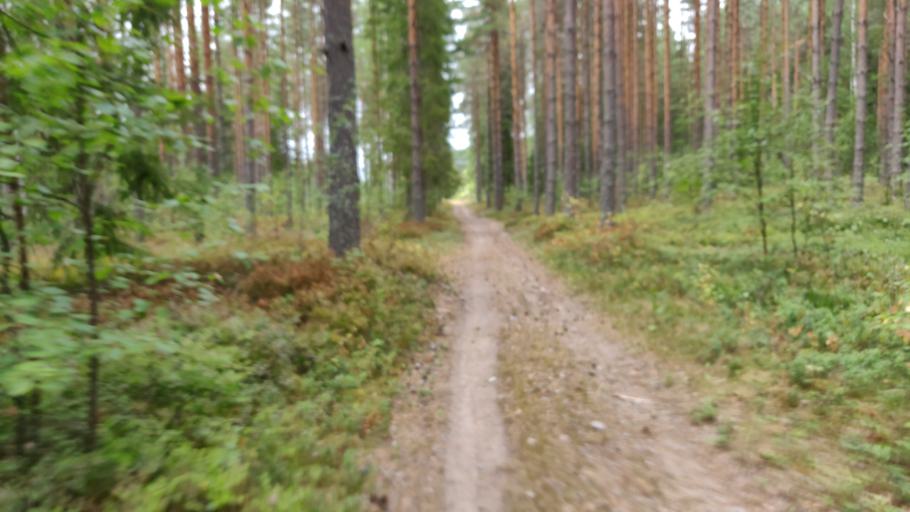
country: SE
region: Vaermland
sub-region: Hagfors Kommun
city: Hagfors
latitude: 60.0378
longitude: 13.5366
